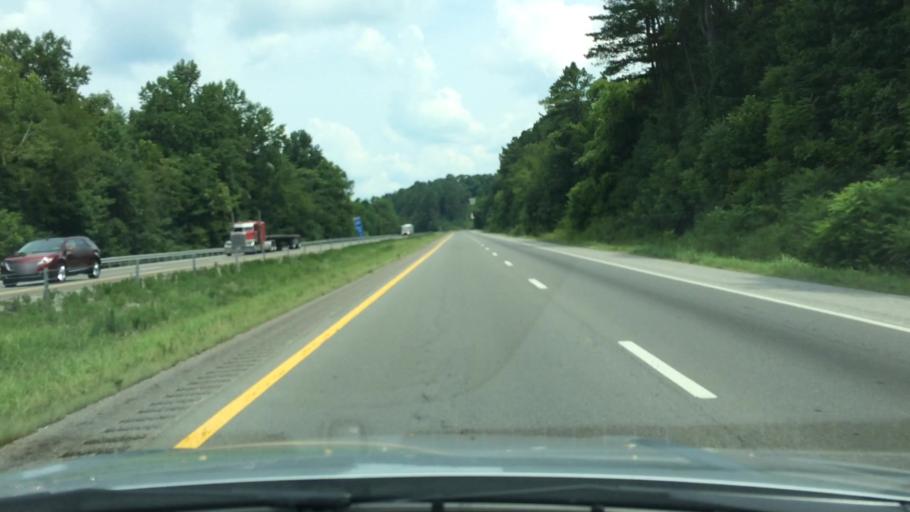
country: US
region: Tennessee
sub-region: Marshall County
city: Cornersville
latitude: 35.2555
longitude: -86.8829
